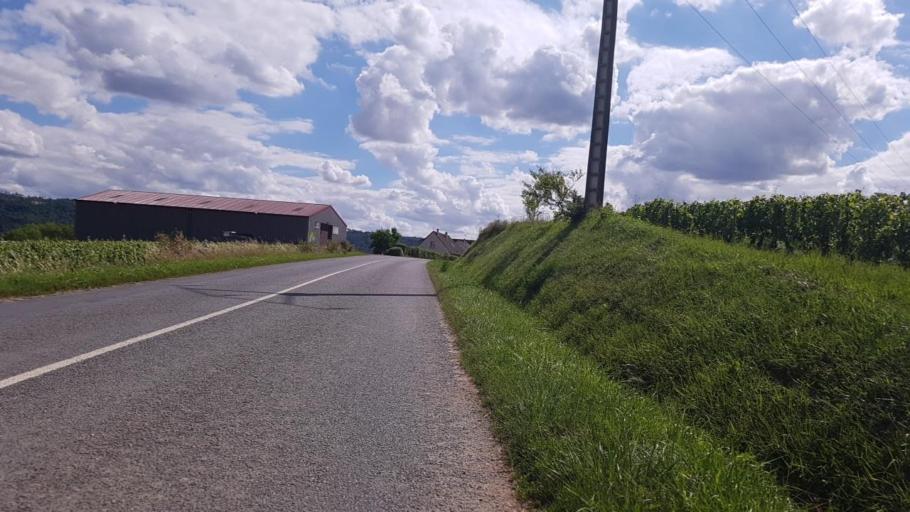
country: FR
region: Champagne-Ardenne
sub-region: Departement de la Marne
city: Dormans
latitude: 49.0697
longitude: 3.5963
